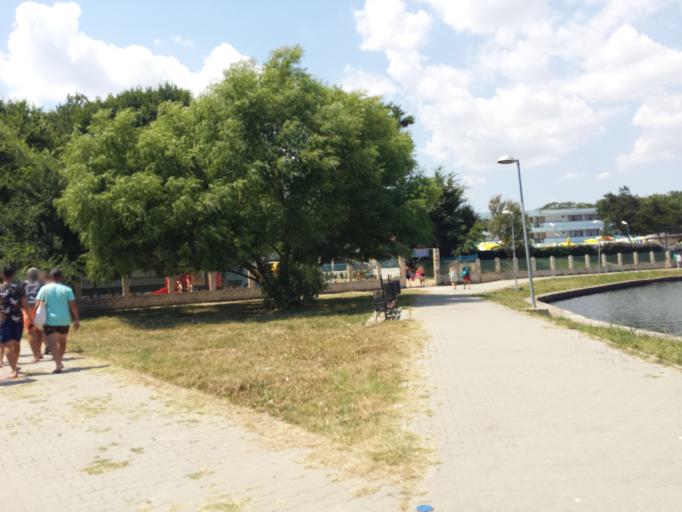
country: RO
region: Constanta
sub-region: Comuna Douazeci si Trei August
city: Douazeci si Trei August
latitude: 43.8600
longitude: 28.6035
